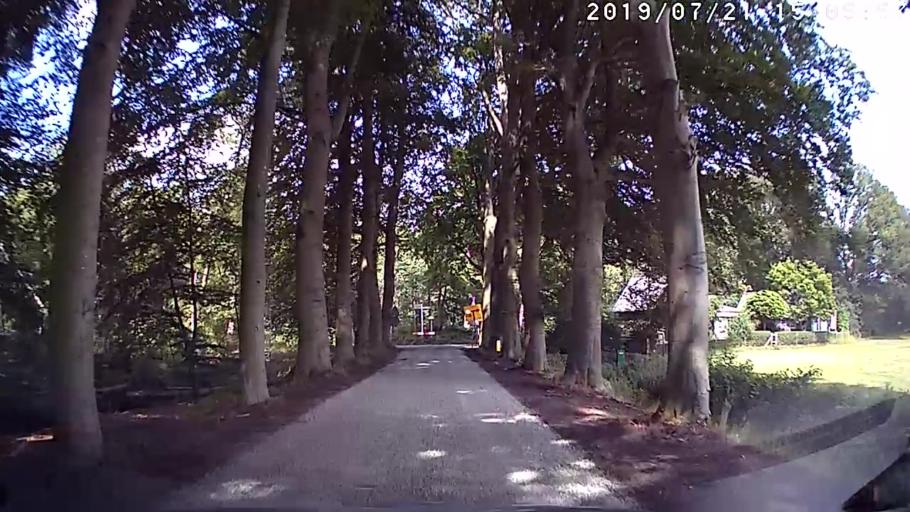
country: NL
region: Overijssel
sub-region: Gemeente Raalte
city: Heino
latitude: 52.4496
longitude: 6.2031
